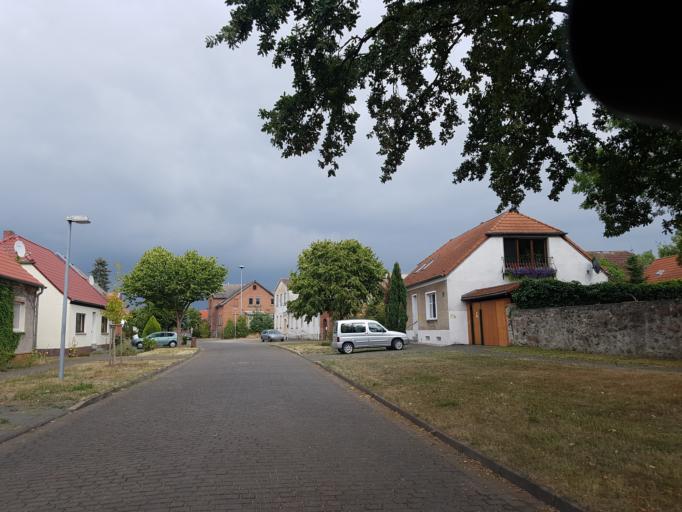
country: DE
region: Brandenburg
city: Gorzke
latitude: 52.0352
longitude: 12.2880
